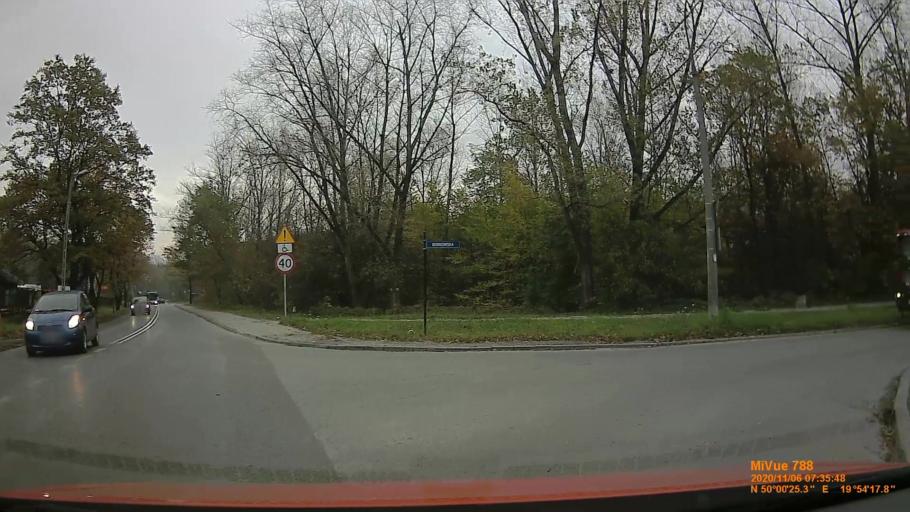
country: PL
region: Lesser Poland Voivodeship
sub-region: Krakow
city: Sidzina
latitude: 50.0070
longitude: 19.9050
